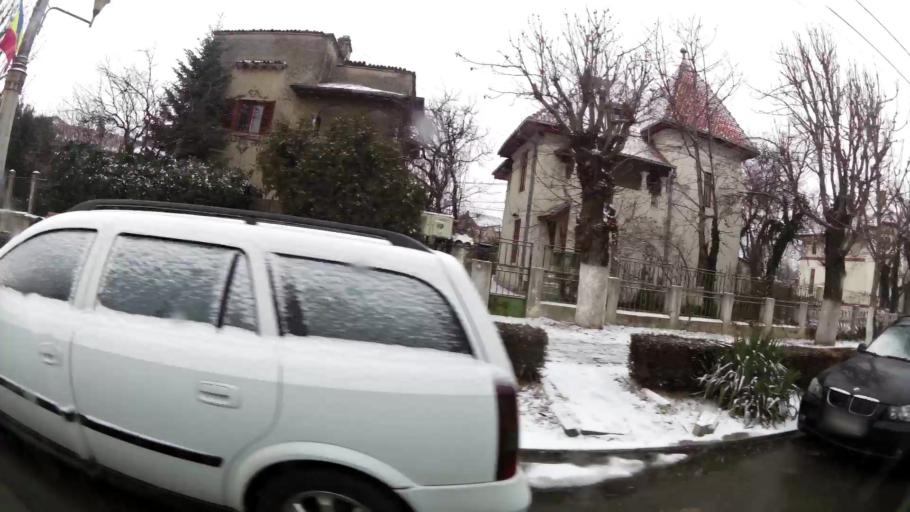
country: RO
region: Dambovita
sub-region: Municipiul Targoviste
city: Targoviste
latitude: 44.9221
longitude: 25.4571
